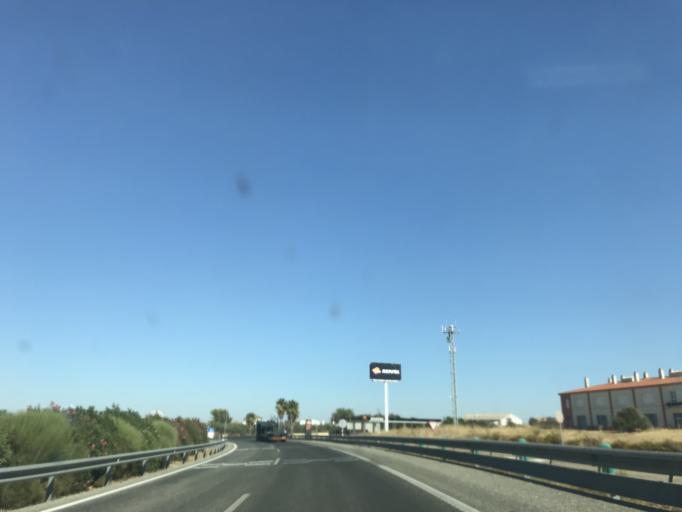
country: ES
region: Andalusia
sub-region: Provincia de Sevilla
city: La Puebla de Cazalla
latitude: 37.2288
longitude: -5.3253
